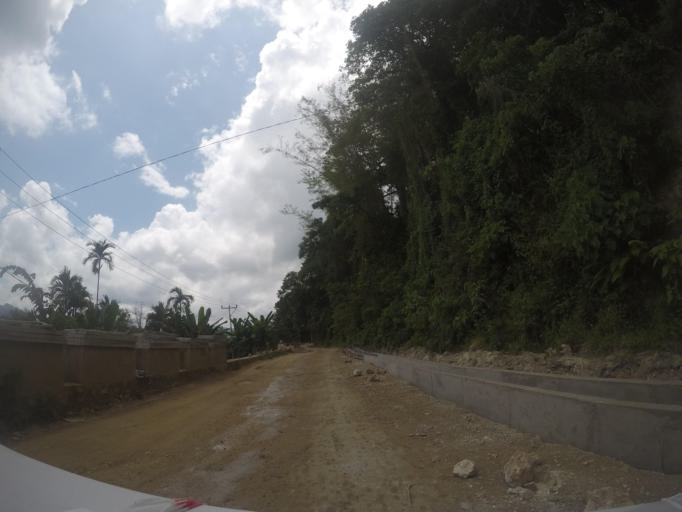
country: TL
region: Baucau
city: Venilale
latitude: -8.6021
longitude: 126.3843
